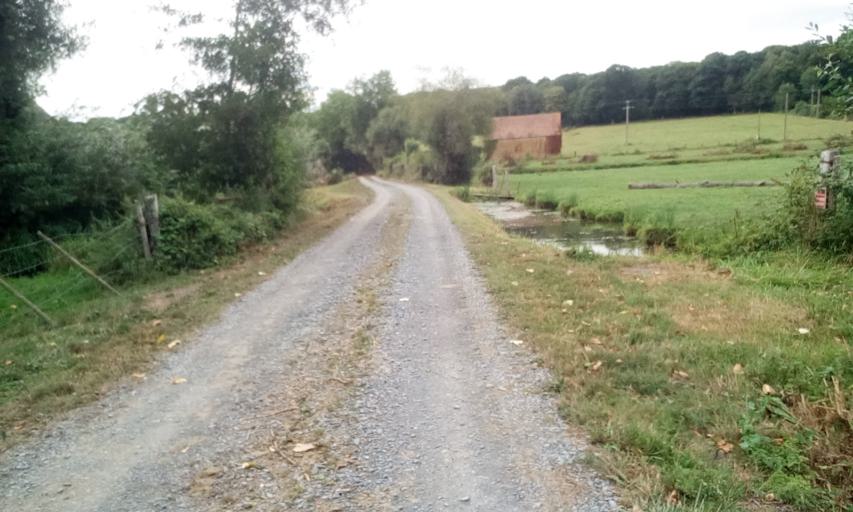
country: FR
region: Lower Normandy
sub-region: Departement du Calvados
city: Bavent
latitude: 49.2147
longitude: -0.1775
